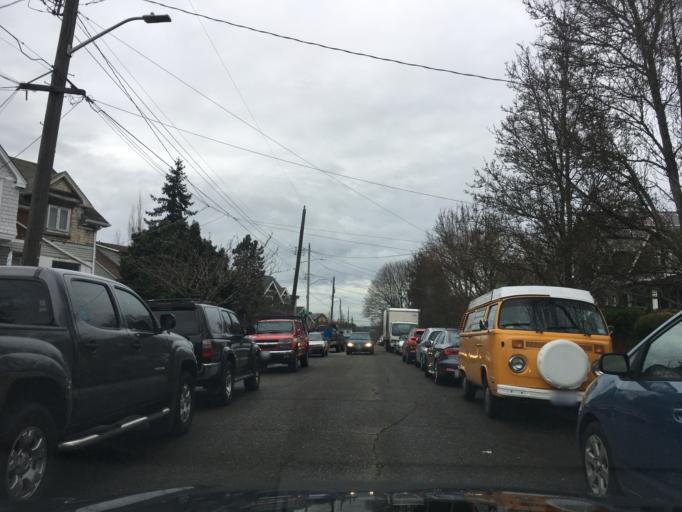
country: US
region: Washington
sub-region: King County
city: Seattle
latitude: 47.6660
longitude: -122.3313
